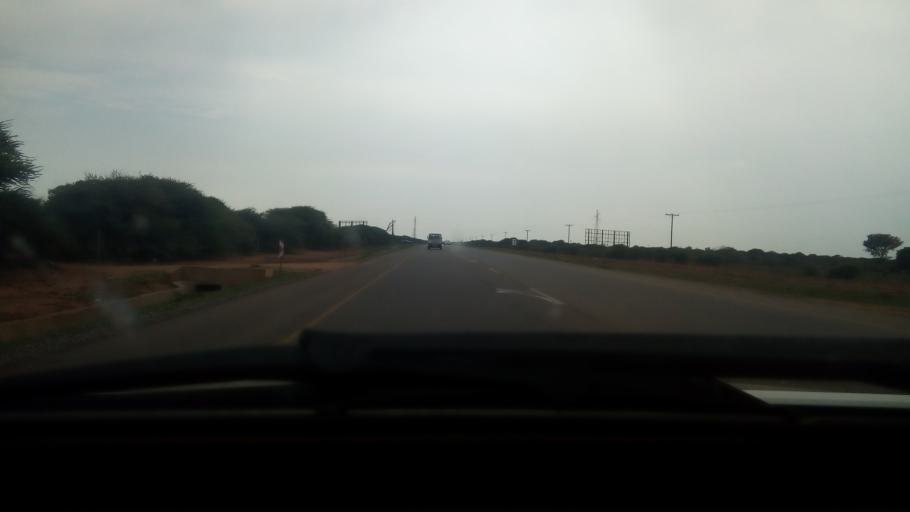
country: BW
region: South East
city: Gaborone
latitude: -24.6713
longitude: 26.0324
